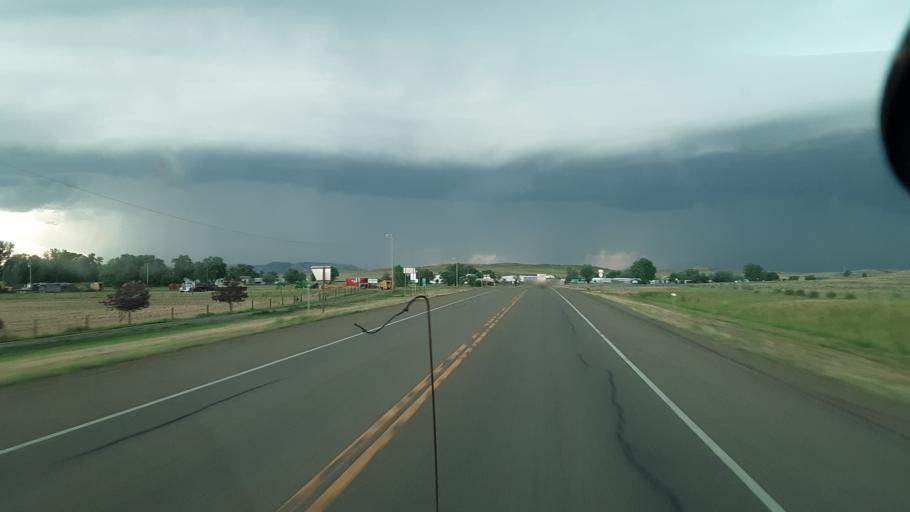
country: US
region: Montana
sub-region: Powder River County
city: Broadus
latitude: 45.4435
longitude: -105.4147
